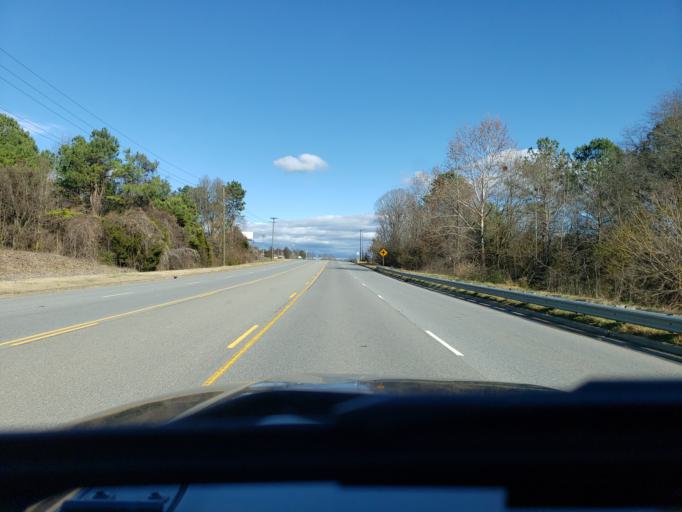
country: US
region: North Carolina
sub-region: Cleveland County
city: Shelby
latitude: 35.2584
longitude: -81.5595
